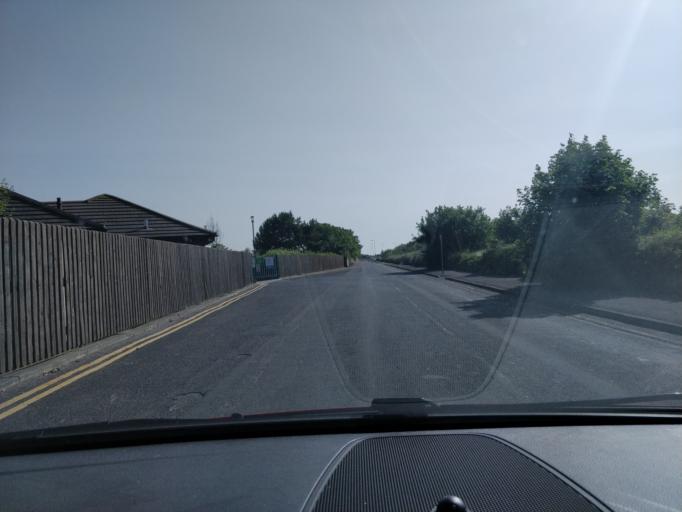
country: GB
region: England
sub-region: Sefton
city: Southport
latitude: 53.6422
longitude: -3.0242
